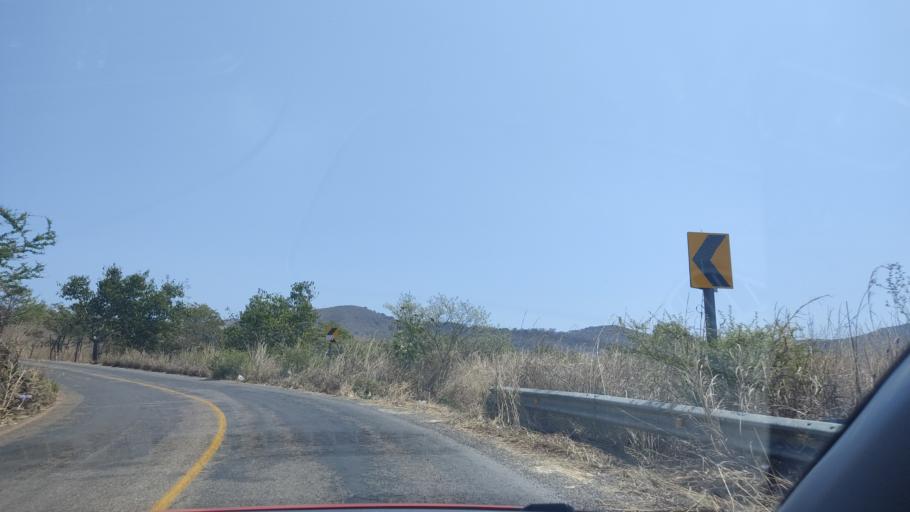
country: MX
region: Nayarit
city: Puga
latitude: 21.5746
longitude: -104.7604
